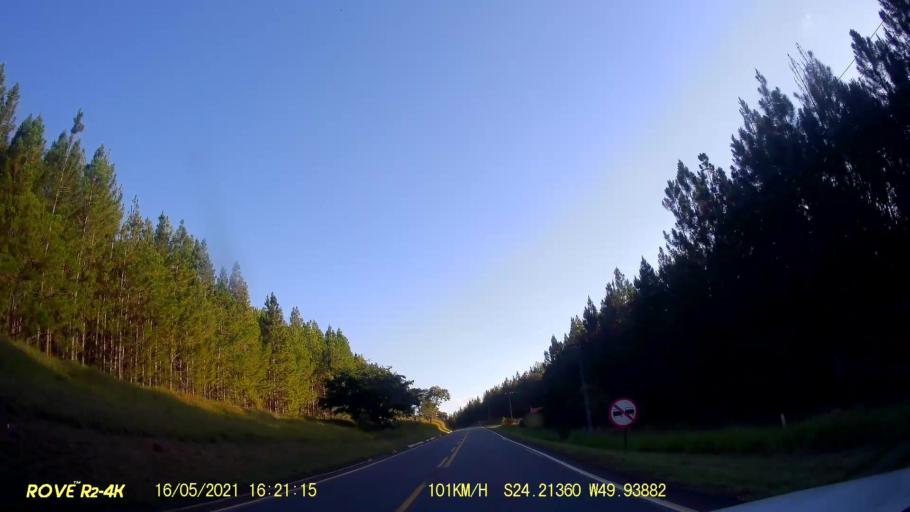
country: BR
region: Parana
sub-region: Jaguariaiva
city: Jaguariaiva
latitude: -24.2137
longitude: -49.9389
